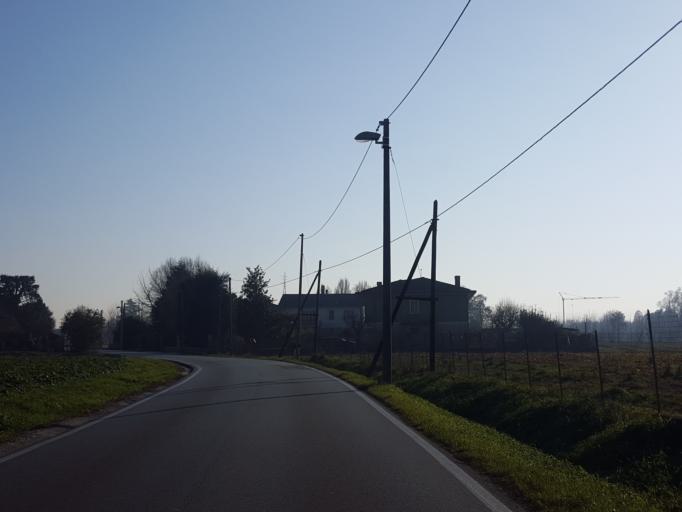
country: IT
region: Veneto
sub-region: Provincia di Vicenza
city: Lisiera
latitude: 45.5632
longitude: 11.5941
